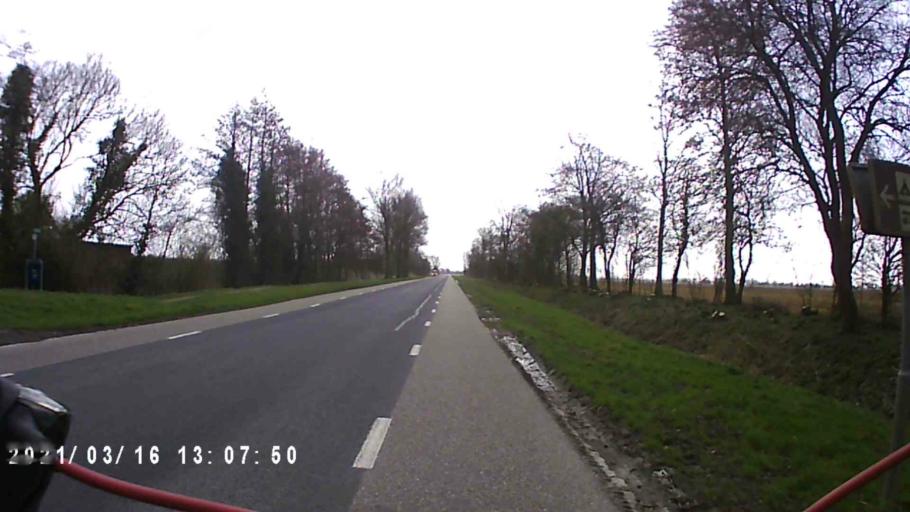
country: NL
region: Friesland
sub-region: Gemeente Het Bildt
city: Minnertsga
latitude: 53.2502
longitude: 5.6209
